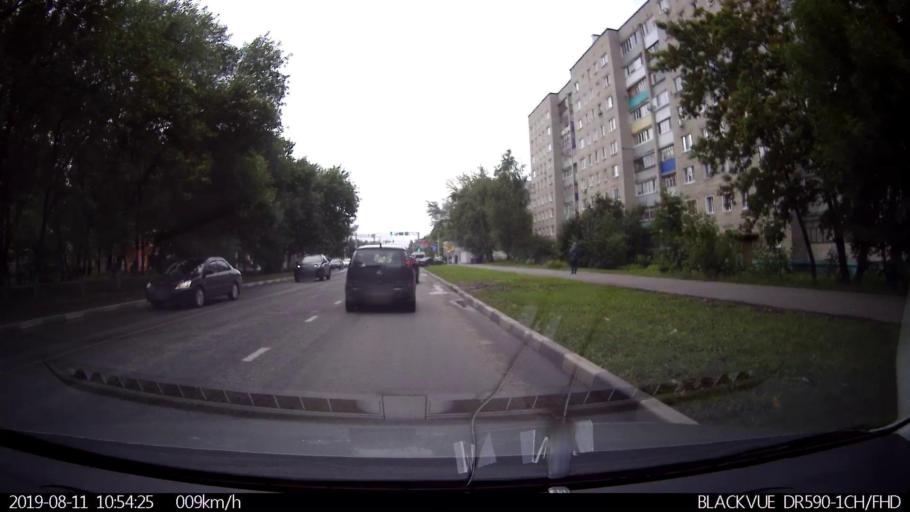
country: RU
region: Ulyanovsk
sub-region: Ulyanovskiy Rayon
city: Ulyanovsk
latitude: 54.2568
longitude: 48.3342
